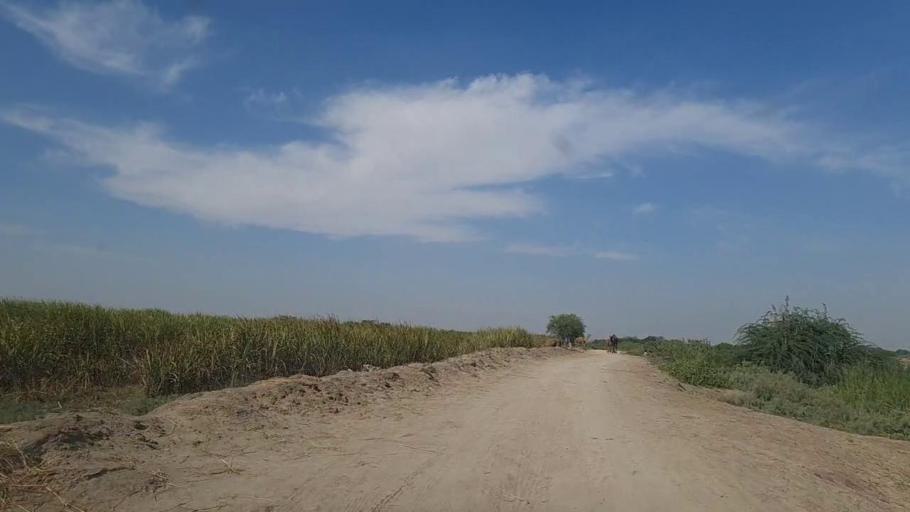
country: PK
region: Sindh
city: Mirpur Batoro
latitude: 24.8038
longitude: 68.2667
